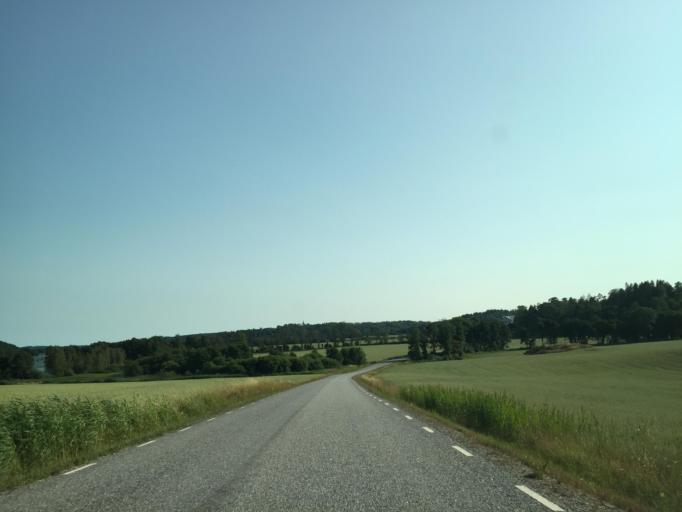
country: SE
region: Vaestra Goetaland
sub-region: Lilla Edets Kommun
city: Lilla Edet
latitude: 58.2020
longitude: 12.1235
